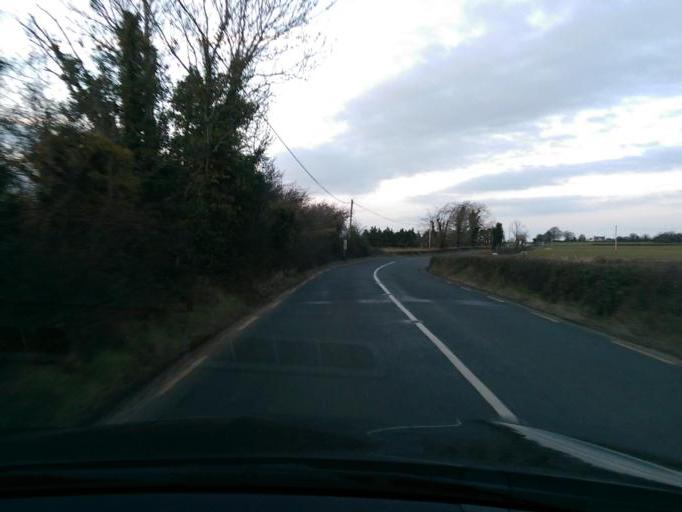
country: IE
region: Connaught
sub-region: County Galway
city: Portumna
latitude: 53.0417
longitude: -8.1135
